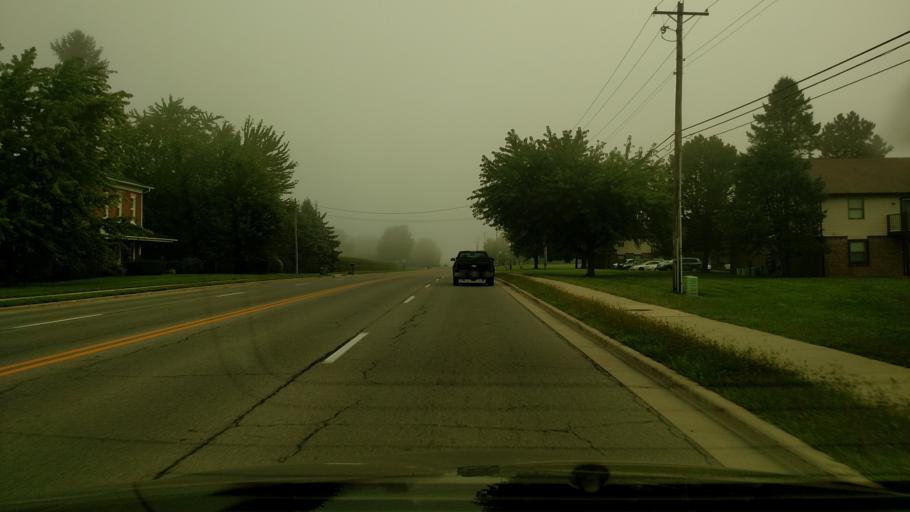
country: US
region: Indiana
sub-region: Howard County
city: Indian Heights
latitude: 40.4485
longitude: -86.1651
